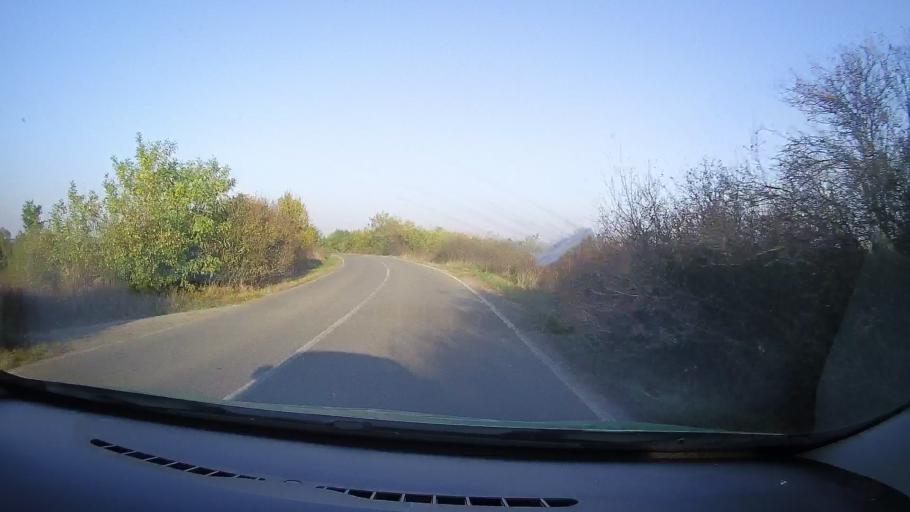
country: RO
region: Arad
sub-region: Comuna Tarnova
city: Chier
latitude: 46.3325
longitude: 21.8676
